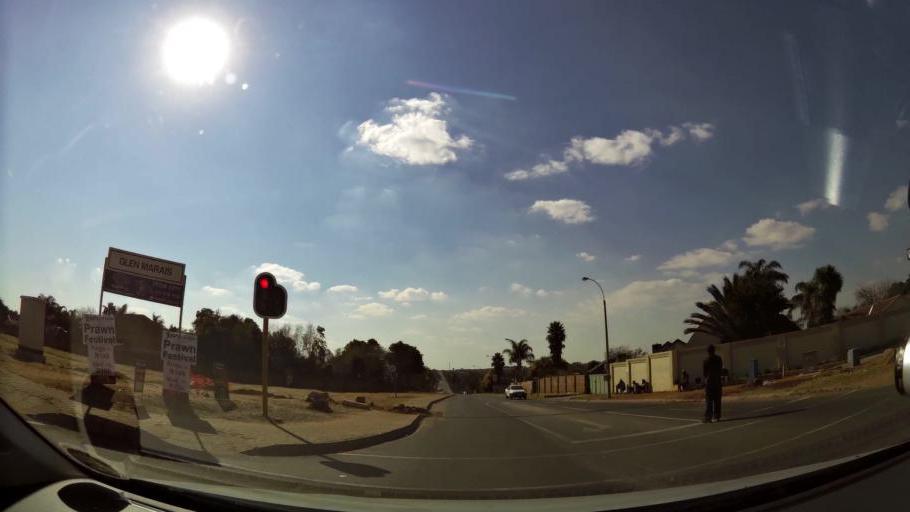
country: ZA
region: Gauteng
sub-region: Ekurhuleni Metropolitan Municipality
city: Tembisa
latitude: -26.0702
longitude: 28.2468
